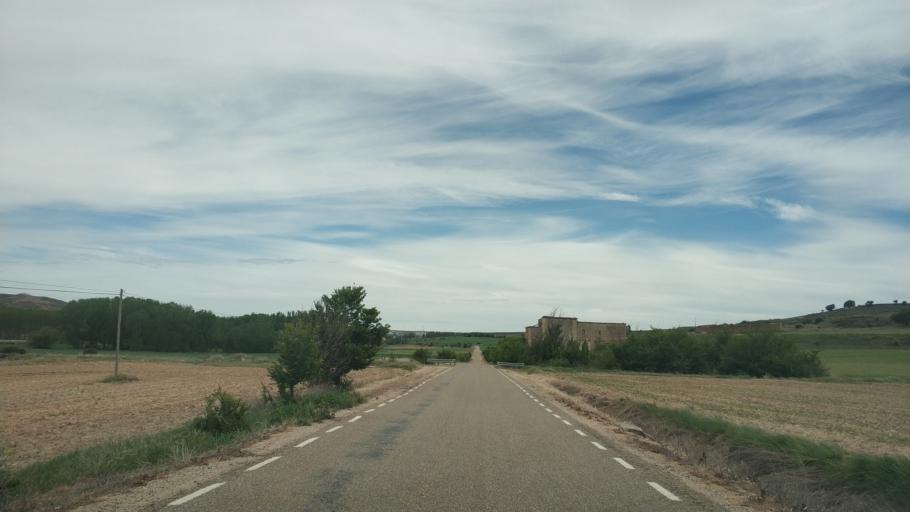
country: ES
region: Castille and Leon
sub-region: Provincia de Soria
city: Berlanga de Duero
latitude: 41.4498
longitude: -2.8399
